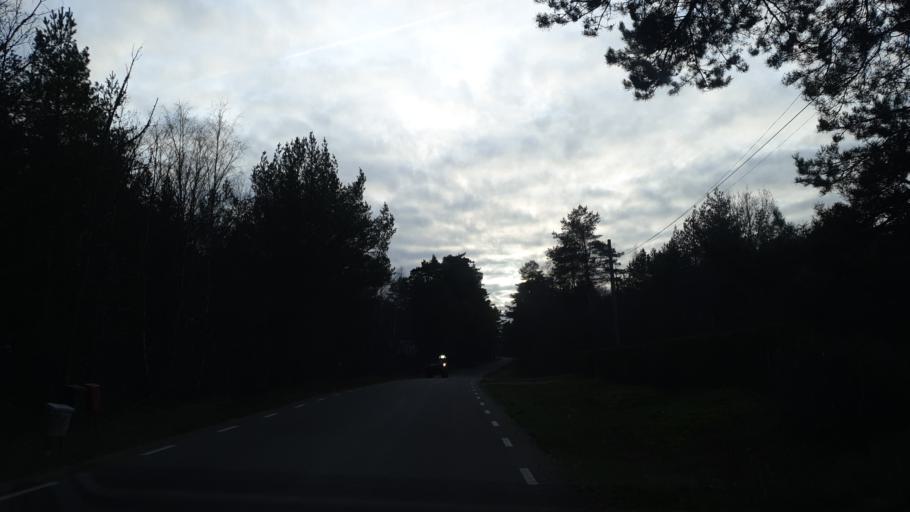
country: SE
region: Kalmar
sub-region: Torsas Kommun
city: Torsas
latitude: 56.2410
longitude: 16.0021
